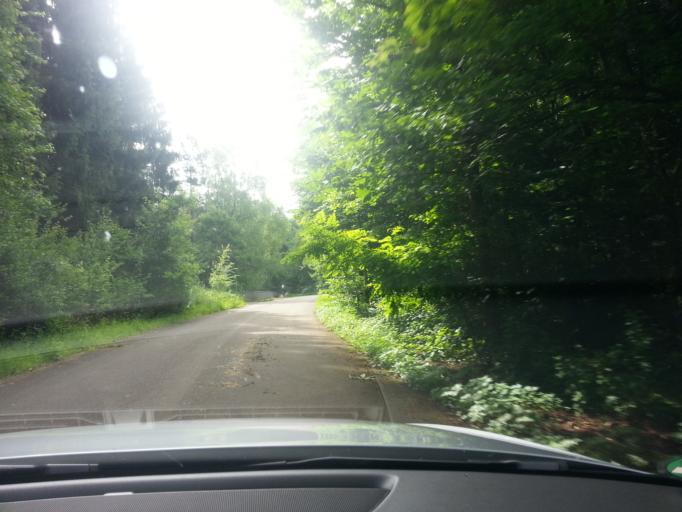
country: DE
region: Saarland
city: Losheim
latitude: 49.5109
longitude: 6.7177
